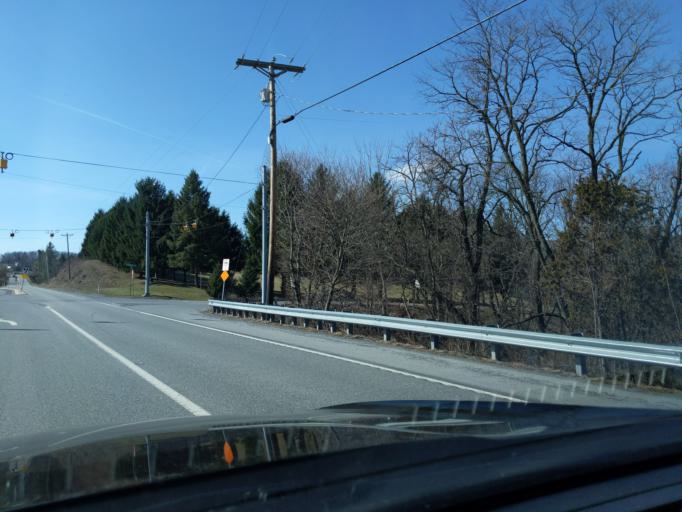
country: US
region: Pennsylvania
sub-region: Blair County
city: Roaring Spring
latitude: 40.3216
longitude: -78.3909
